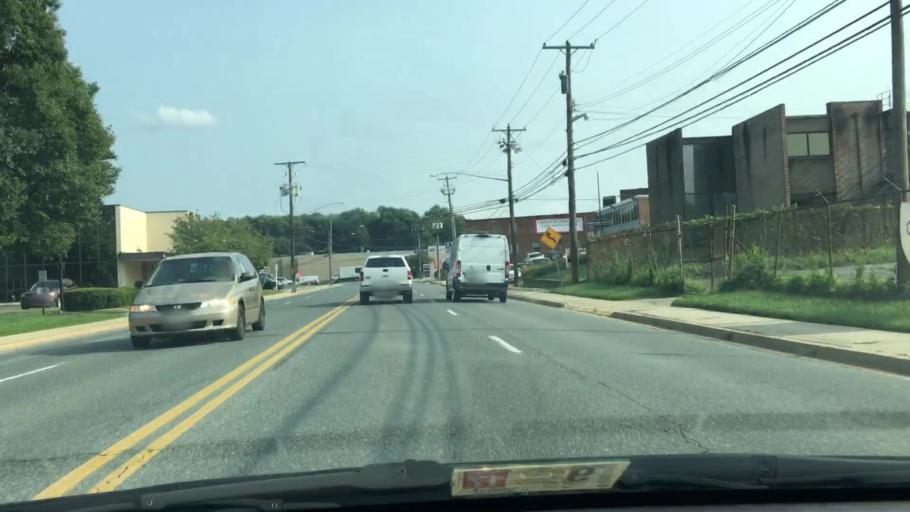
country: US
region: Maryland
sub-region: Montgomery County
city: North Bethesda
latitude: 39.0587
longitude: -77.1108
